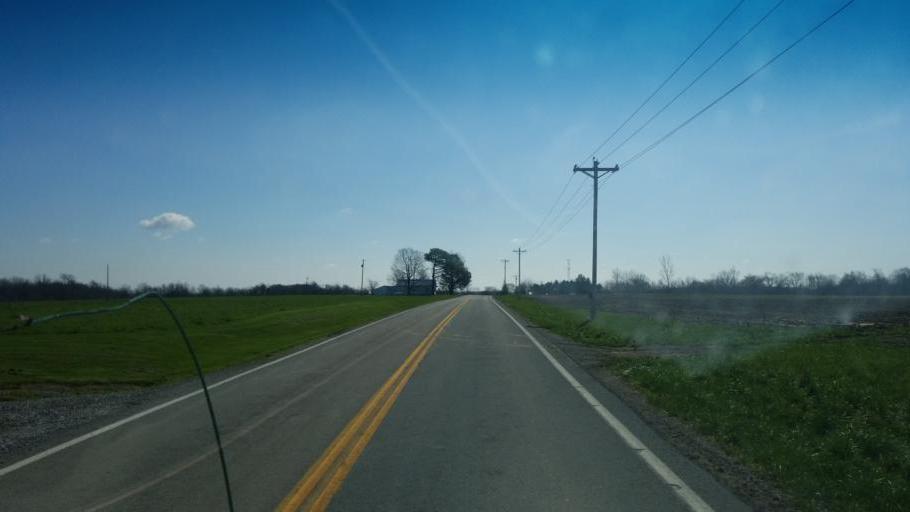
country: US
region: Ohio
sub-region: Wyandot County
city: Upper Sandusky
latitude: 40.7381
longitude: -83.3838
